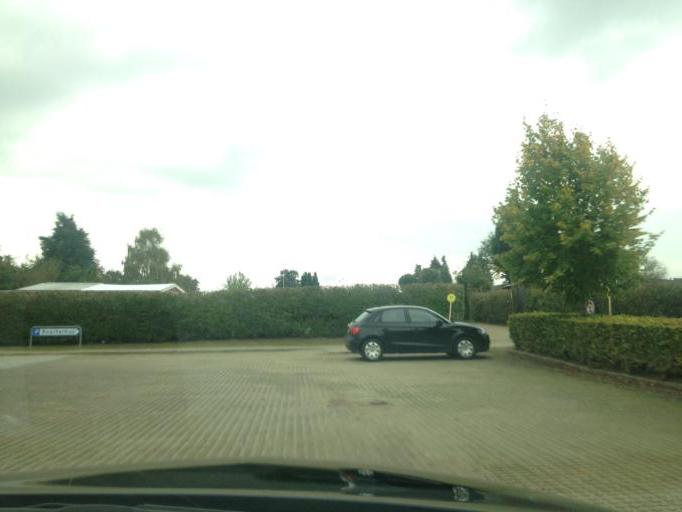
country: DK
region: South Denmark
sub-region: Kolding Kommune
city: Kolding
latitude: 55.4767
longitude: 9.4600
